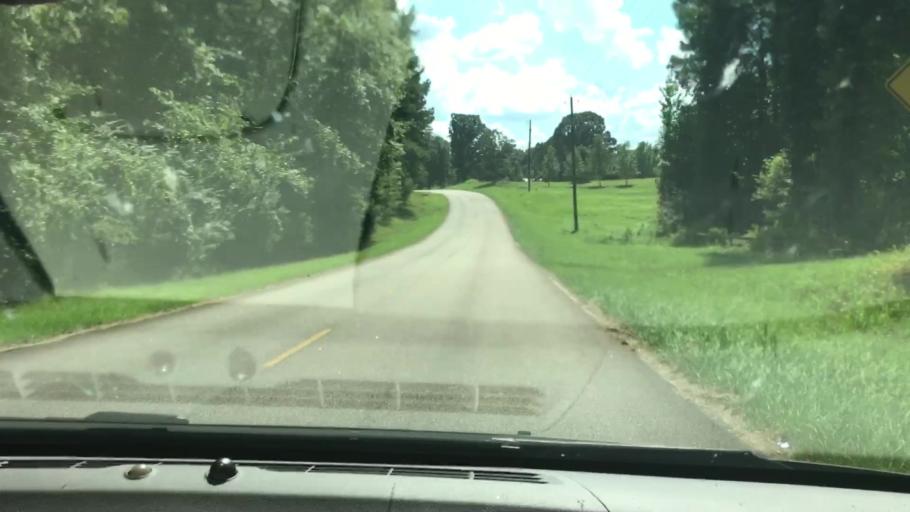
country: US
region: Georgia
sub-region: Troup County
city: La Grange
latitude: 33.1116
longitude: -85.1268
